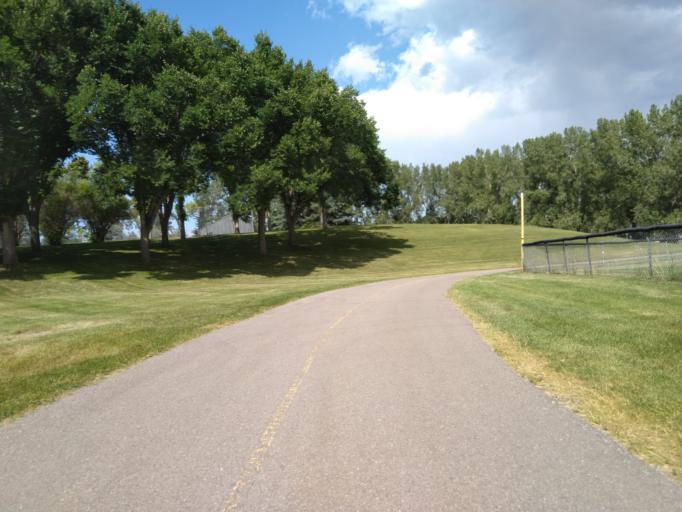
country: CA
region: Alberta
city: Calgary
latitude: 51.0805
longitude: -114.0790
